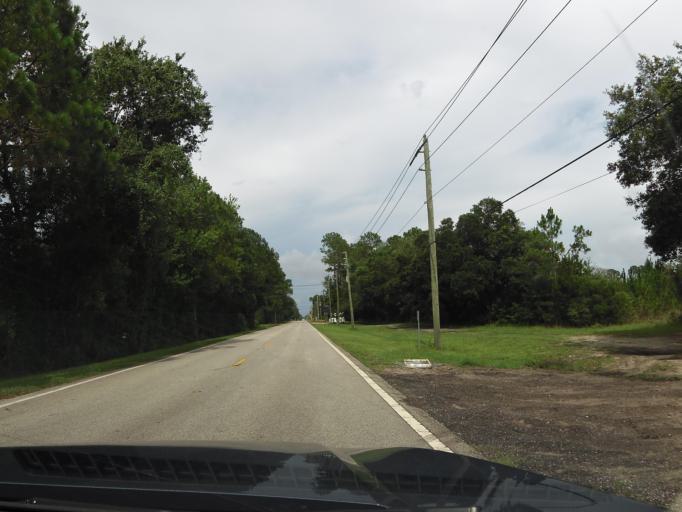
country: US
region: Florida
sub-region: Saint Johns County
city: Saint Augustine South
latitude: 29.8590
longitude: -81.4178
